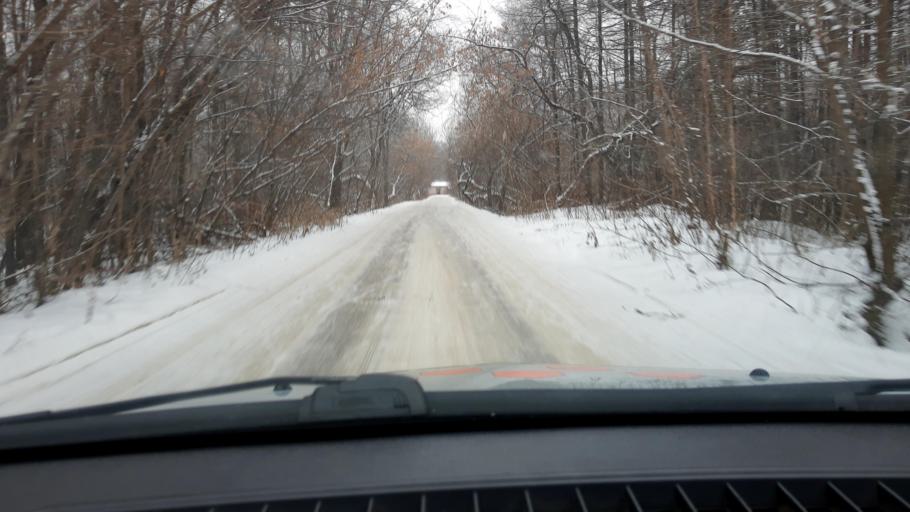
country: RU
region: Bashkortostan
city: Iglino
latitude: 54.8189
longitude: 56.1931
